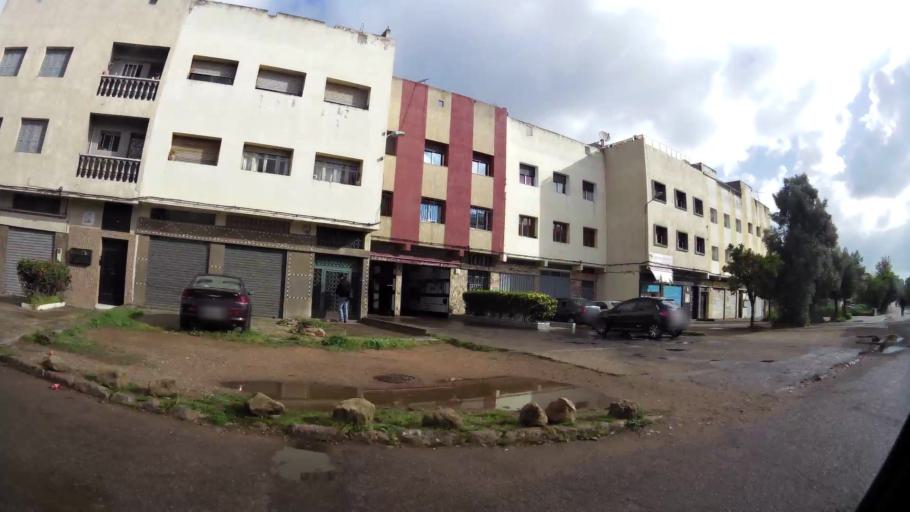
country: MA
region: Grand Casablanca
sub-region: Casablanca
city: Casablanca
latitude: 33.5578
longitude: -7.6833
